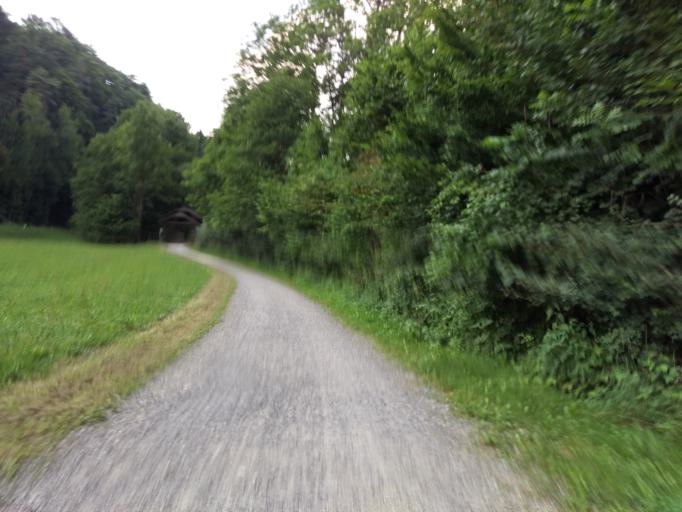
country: AT
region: Styria
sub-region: Politischer Bezirk Graz-Umgebung
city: Thal
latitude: 47.0889
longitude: 15.3740
